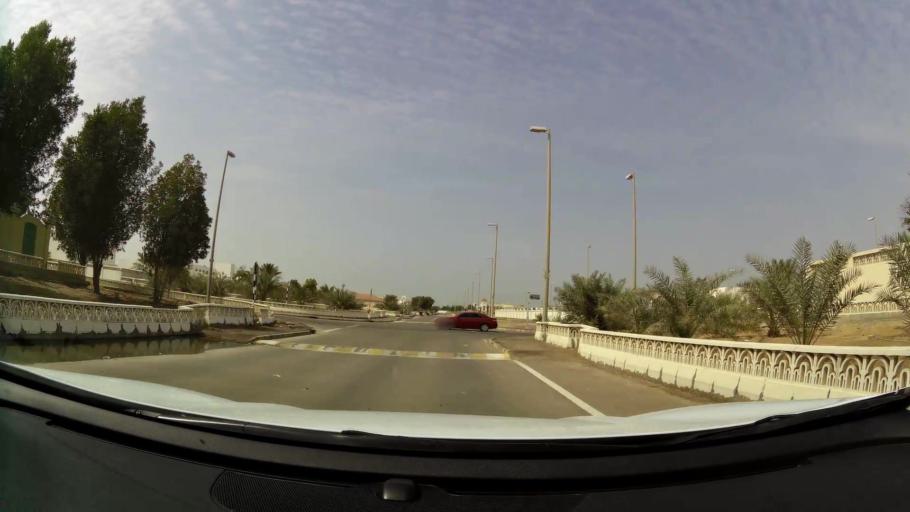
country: AE
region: Abu Dhabi
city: Abu Dhabi
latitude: 24.5186
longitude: 54.6629
